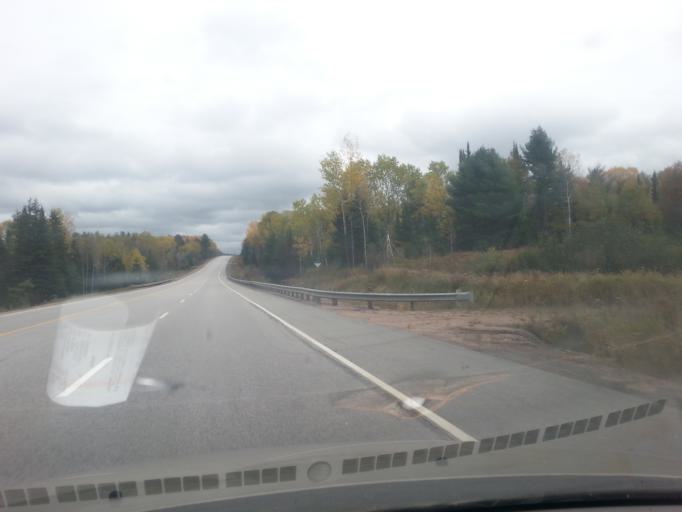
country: CA
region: Ontario
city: Mattawa
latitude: 46.2805
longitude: -78.4308
